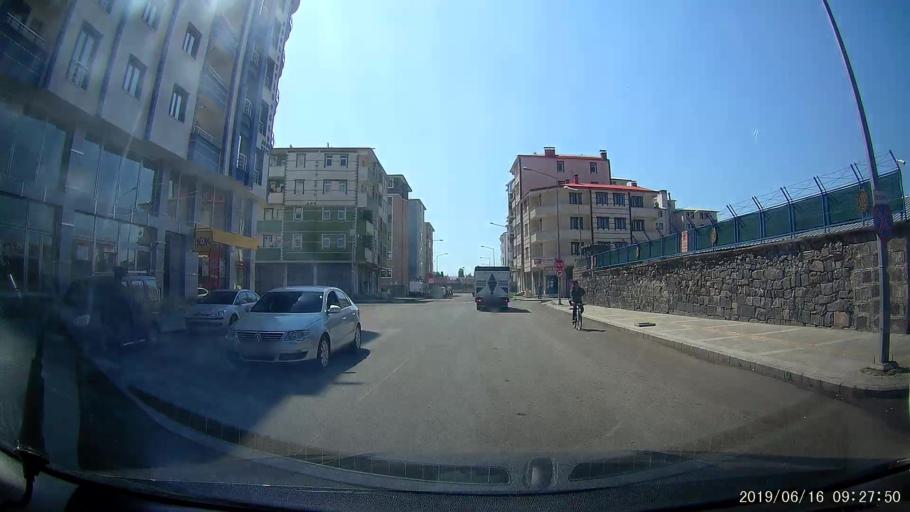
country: TR
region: Kars
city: Kars
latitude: 40.6046
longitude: 43.1029
